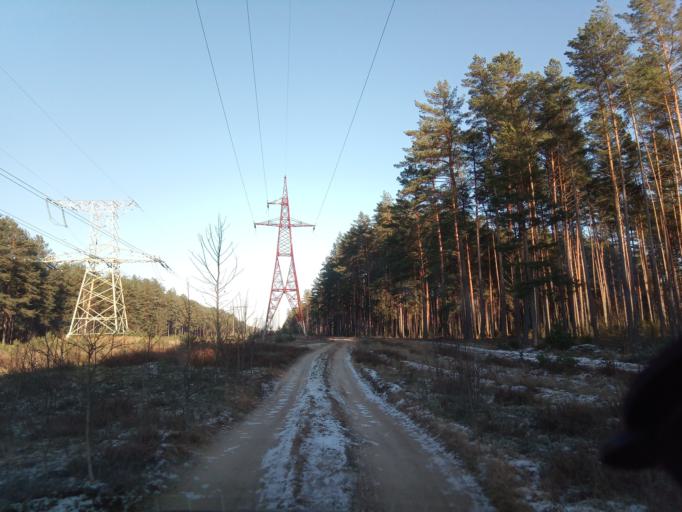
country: LT
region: Alytaus apskritis
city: Druskininkai
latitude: 53.9565
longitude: 23.8633
